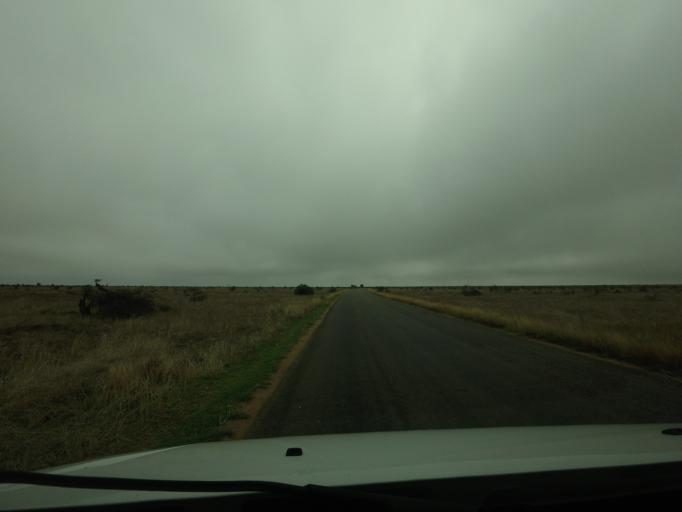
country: ZA
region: Limpopo
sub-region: Mopani District Municipality
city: Phalaborwa
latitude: -24.2337
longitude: 31.7202
